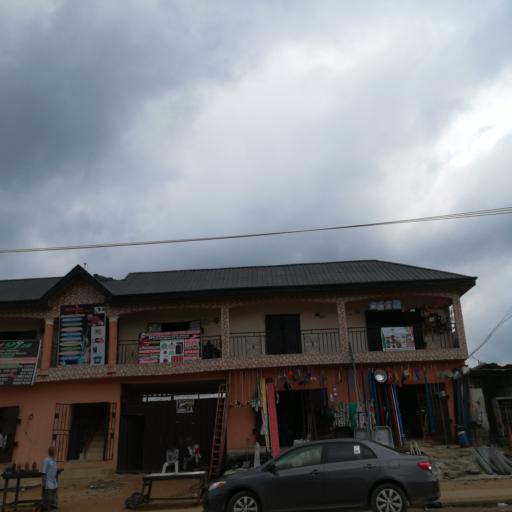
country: NG
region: Rivers
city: Port Harcourt
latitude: 4.8309
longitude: 7.0704
